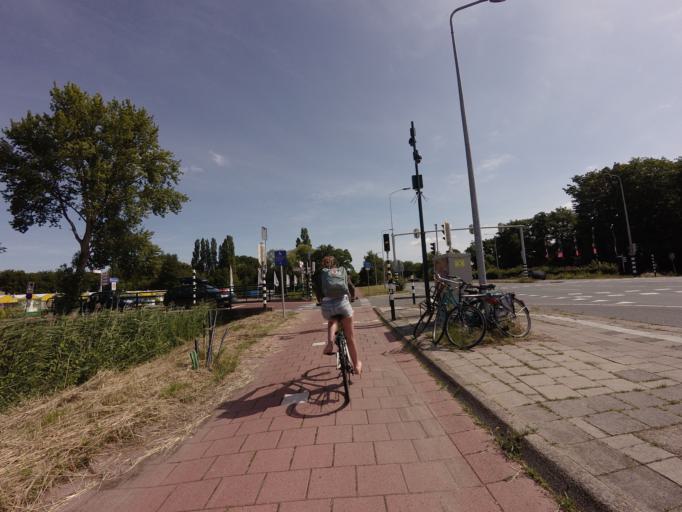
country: NL
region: South Holland
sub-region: Gemeente Leidschendam-Voorburg
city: Voorburg
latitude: 52.0992
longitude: 4.3464
